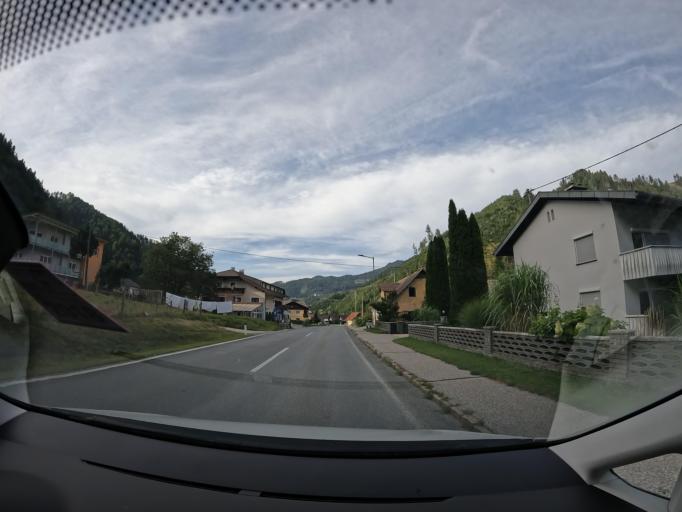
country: AT
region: Carinthia
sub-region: Politischer Bezirk Volkermarkt
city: Bad Eisenkappel
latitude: 46.4718
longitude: 14.5929
